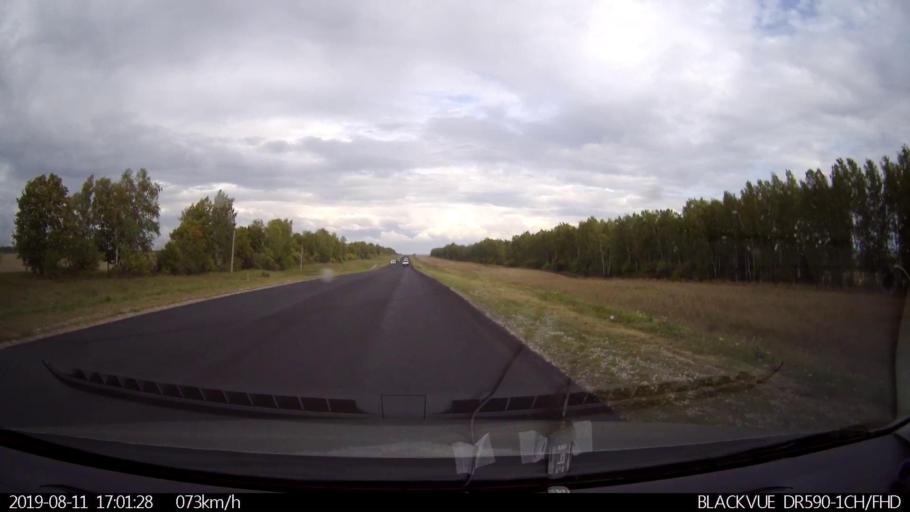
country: RU
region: Ulyanovsk
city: Mayna
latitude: 54.3083
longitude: 47.6977
